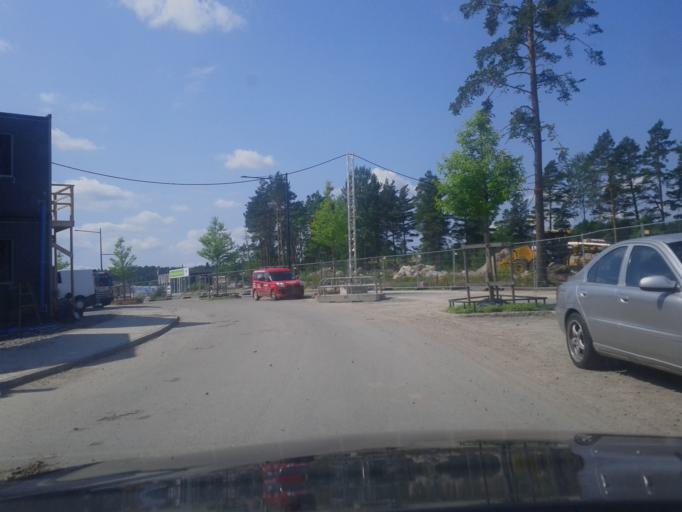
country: SE
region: Stockholm
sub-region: Taby Kommun
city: Taby
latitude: 59.4743
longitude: 18.1263
